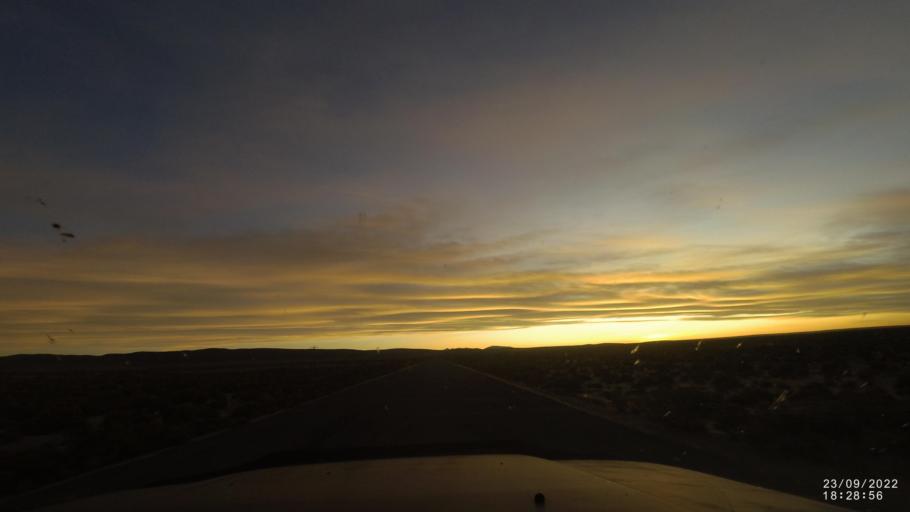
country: BO
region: Oruro
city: Challapata
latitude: -19.3414
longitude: -67.1847
